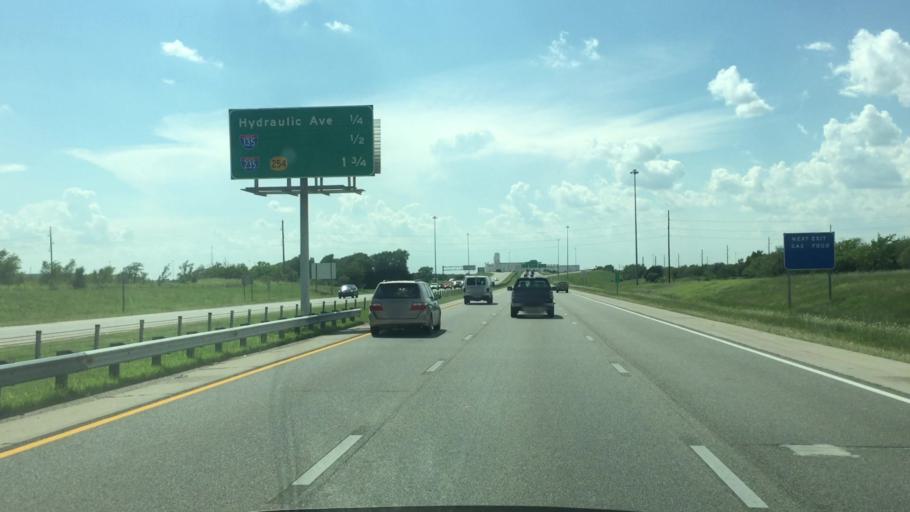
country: US
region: Kansas
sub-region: Sedgwick County
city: Bellaire
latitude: 37.7431
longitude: -97.3064
